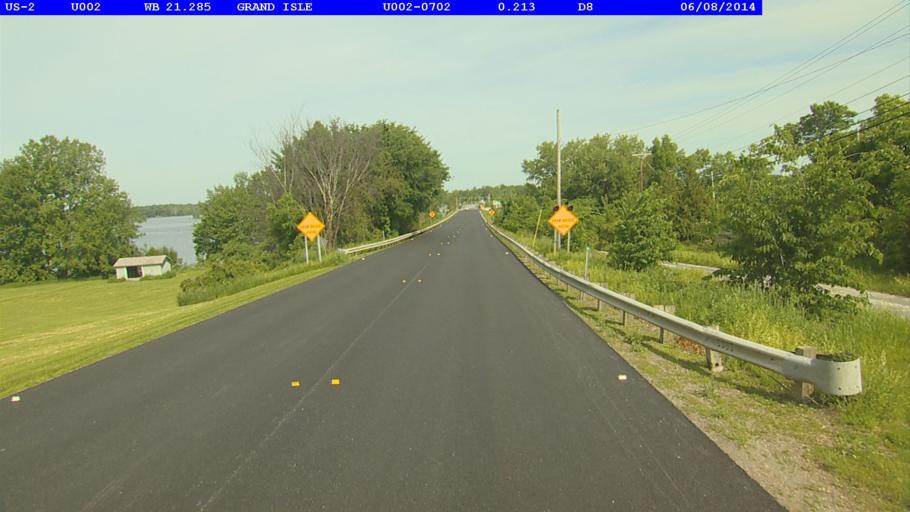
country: US
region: Vermont
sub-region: Grand Isle County
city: North Hero
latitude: 44.7639
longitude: -73.2871
